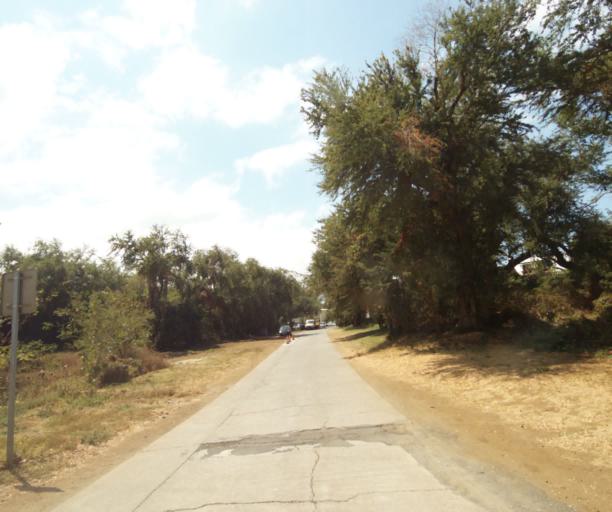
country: RE
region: Reunion
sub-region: Reunion
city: Trois-Bassins
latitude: -21.0912
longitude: 55.2377
